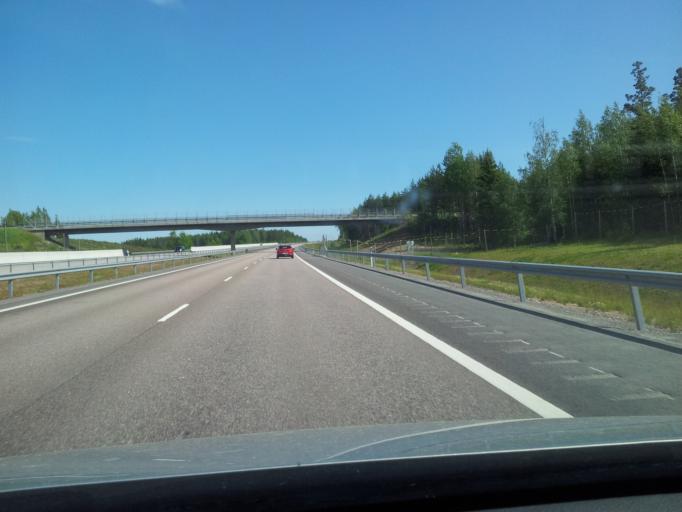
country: FI
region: Uusimaa
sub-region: Loviisa
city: Perna
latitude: 60.4736
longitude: 26.1170
